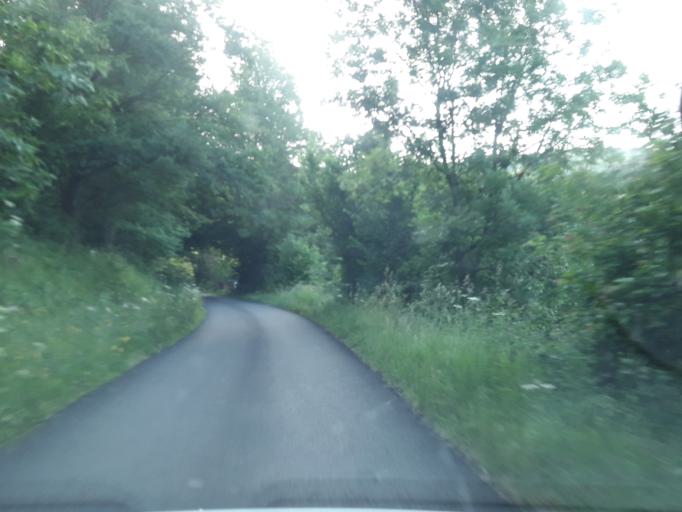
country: FR
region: Rhone-Alpes
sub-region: Departement du Rhone
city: Bessenay
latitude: 45.7576
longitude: 4.5240
